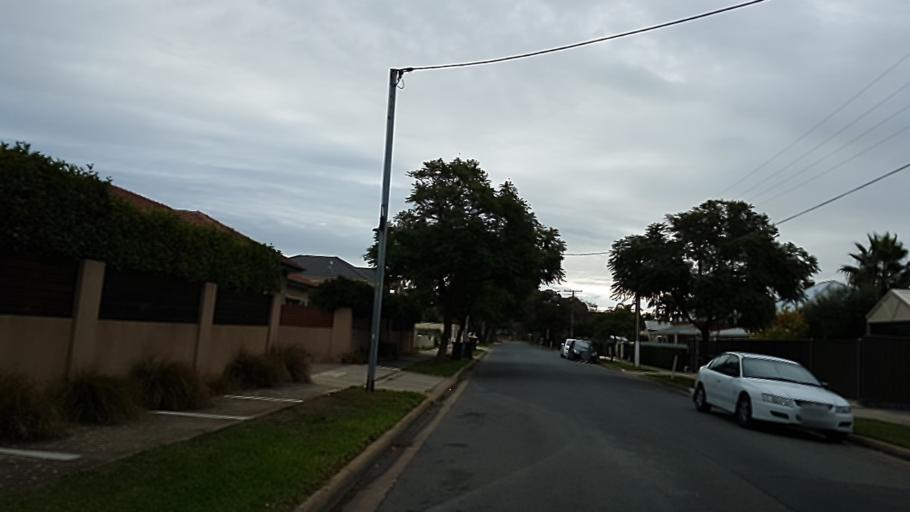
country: AU
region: South Australia
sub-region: Charles Sturt
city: Woodville North
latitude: -34.8769
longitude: 138.5468
